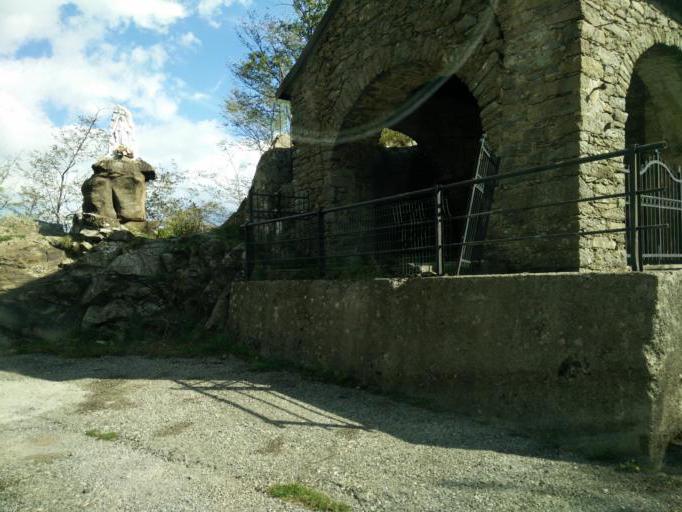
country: IT
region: Tuscany
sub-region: Provincia di Massa-Carrara
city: Patigno
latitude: 44.3476
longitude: 9.7121
